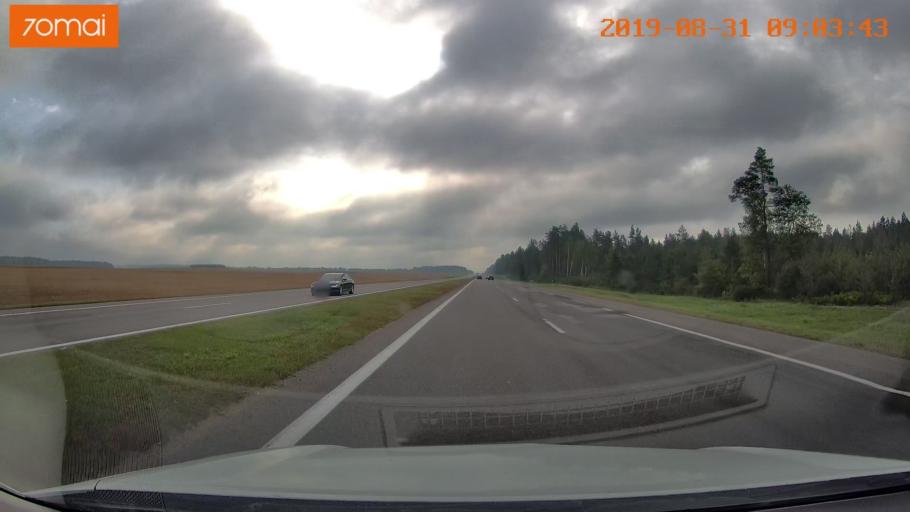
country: BY
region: Minsk
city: Chervyen'
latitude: 53.7379
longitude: 28.3251
